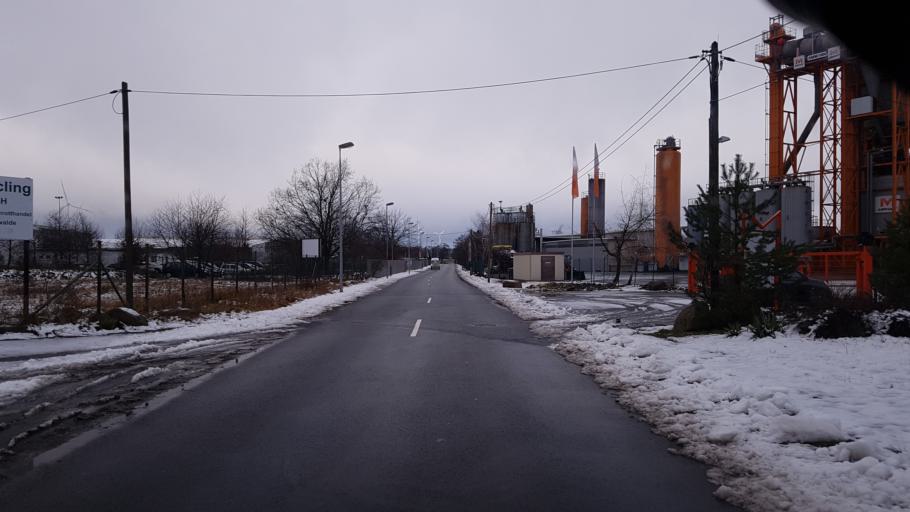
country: DE
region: Brandenburg
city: Luckau
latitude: 51.8771
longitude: 13.7977
